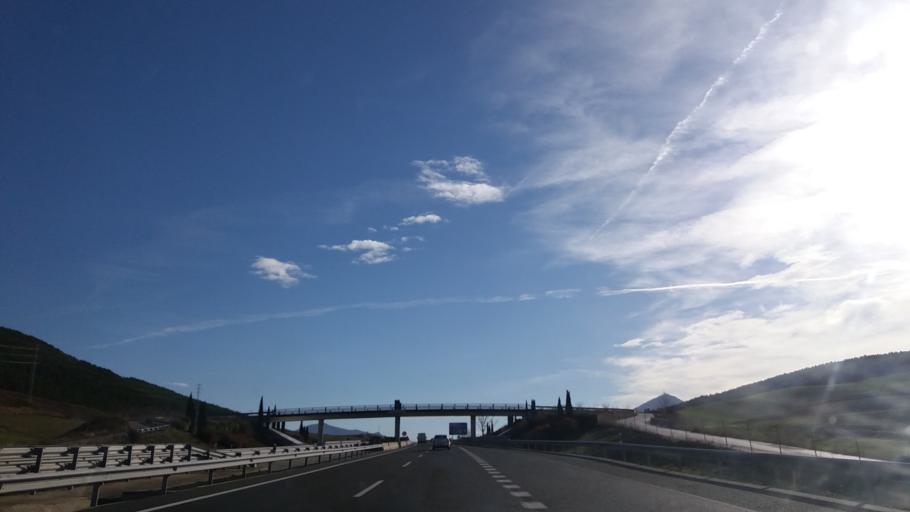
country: ES
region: Navarre
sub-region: Provincia de Navarra
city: Beriain
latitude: 42.7548
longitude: -1.6179
